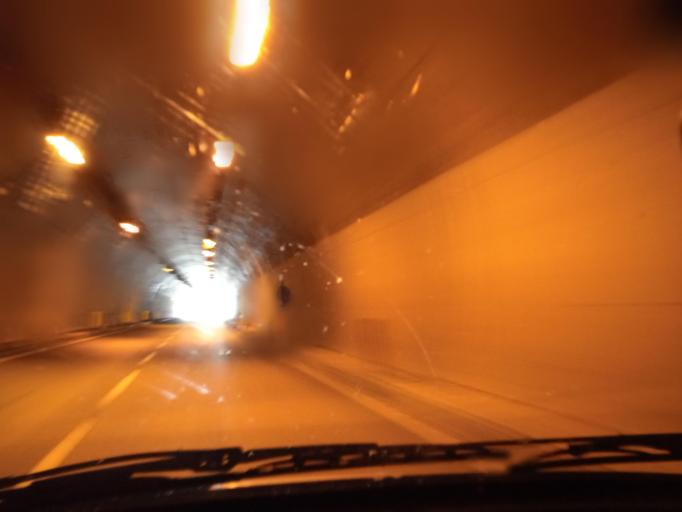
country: IT
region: Sicily
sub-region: Messina
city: Acquedolci
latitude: 38.0544
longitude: 14.6065
